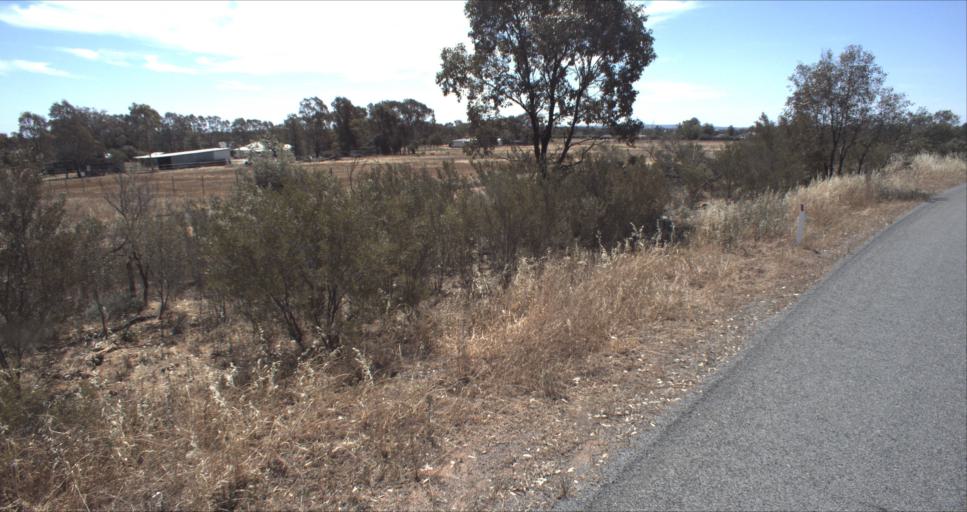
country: AU
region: New South Wales
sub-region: Leeton
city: Leeton
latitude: -34.5828
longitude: 146.4296
